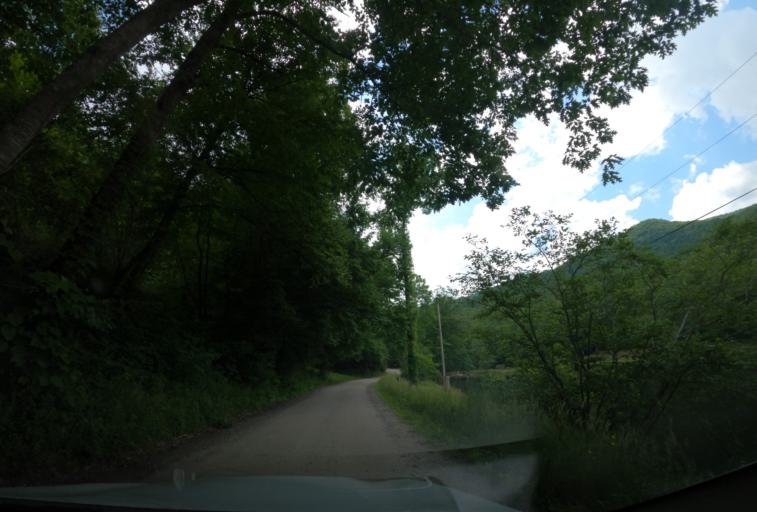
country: US
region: North Carolina
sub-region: Haywood County
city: Hazelwood
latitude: 35.3919
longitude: -82.8967
